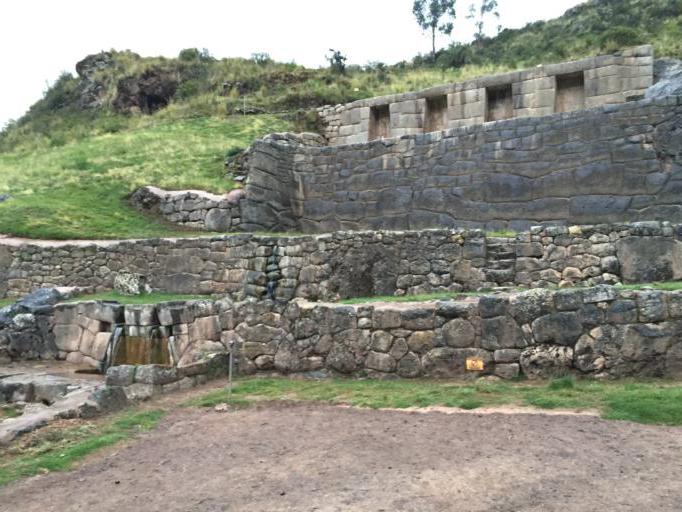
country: PE
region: Cusco
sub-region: Provincia de Cusco
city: Cusco
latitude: -13.4790
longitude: -71.9673
